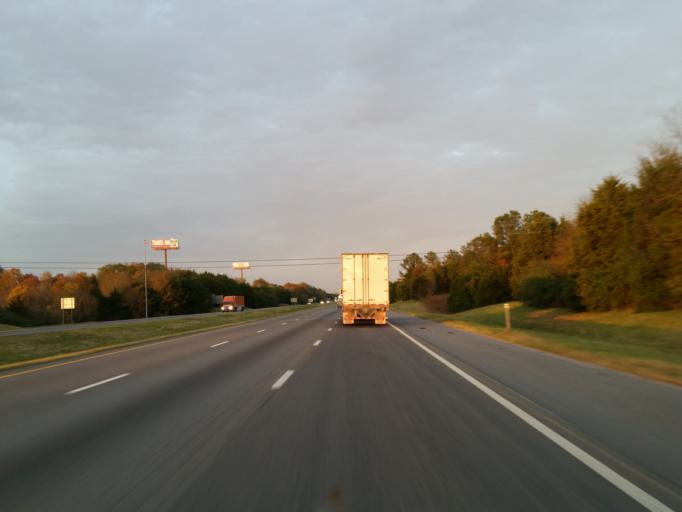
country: US
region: Alabama
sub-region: Sumter County
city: Livingston
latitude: 32.6289
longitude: -88.2063
